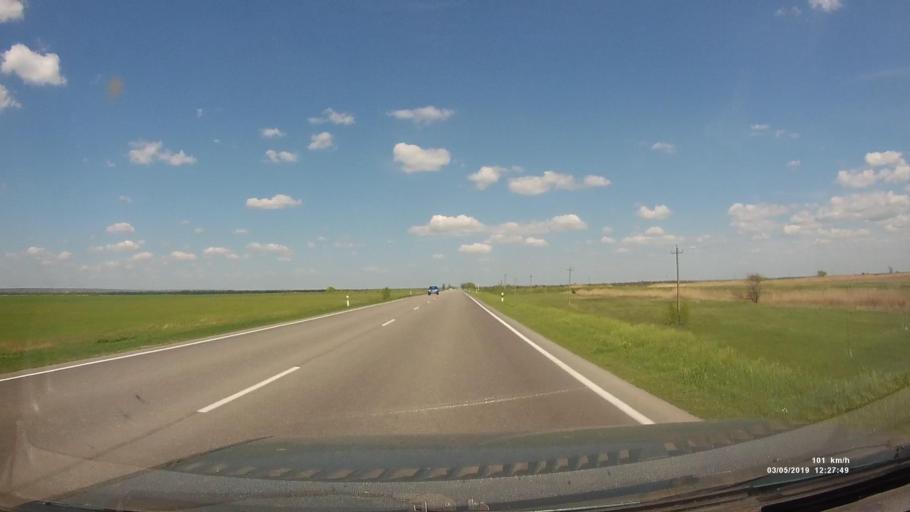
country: RU
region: Rostov
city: Semikarakorsk
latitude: 47.4642
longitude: 40.7235
